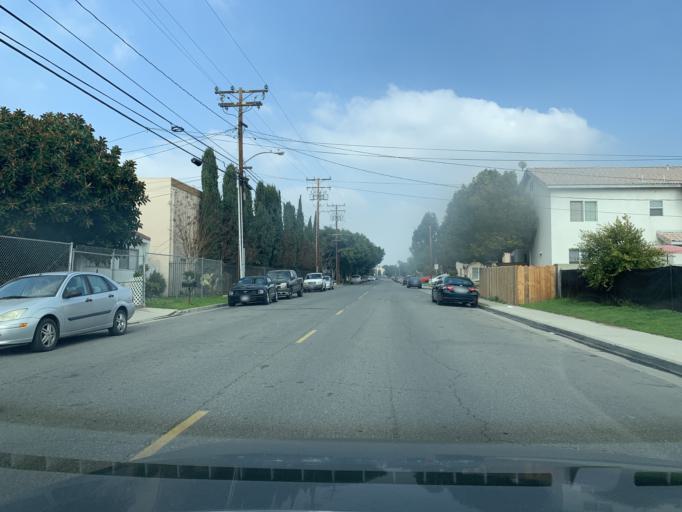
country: US
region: California
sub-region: Los Angeles County
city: South El Monte
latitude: 34.0559
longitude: -118.0492
